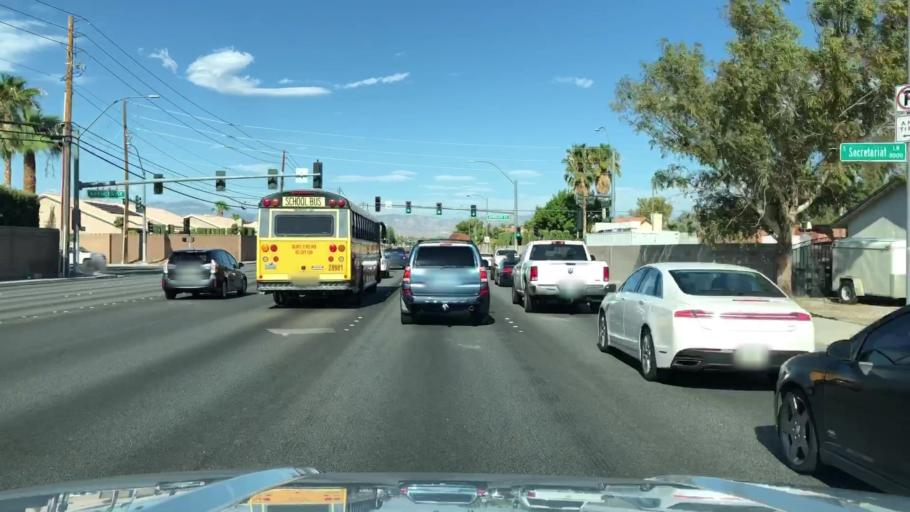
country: US
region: Nevada
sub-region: Clark County
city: Whitney
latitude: 36.0426
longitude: -115.1265
